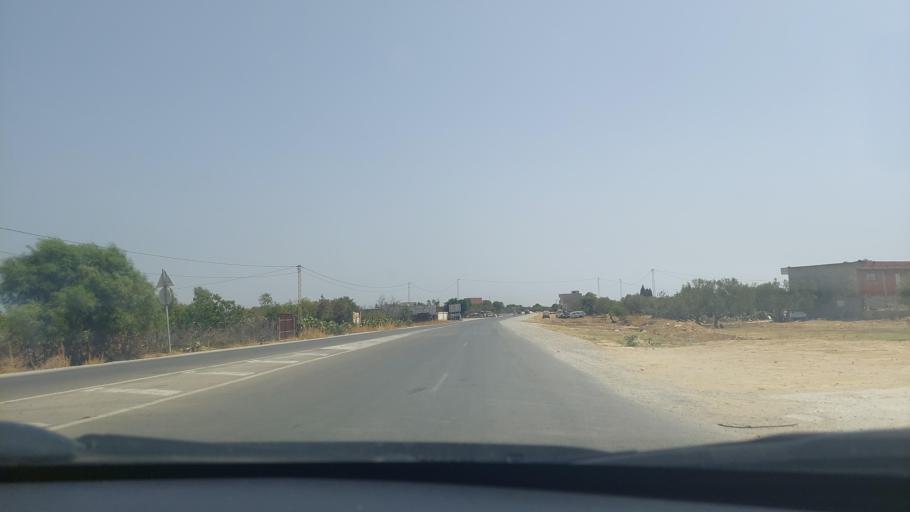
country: TN
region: Al Munastir
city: Qasr Hallal
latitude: 35.6034
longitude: 10.8923
